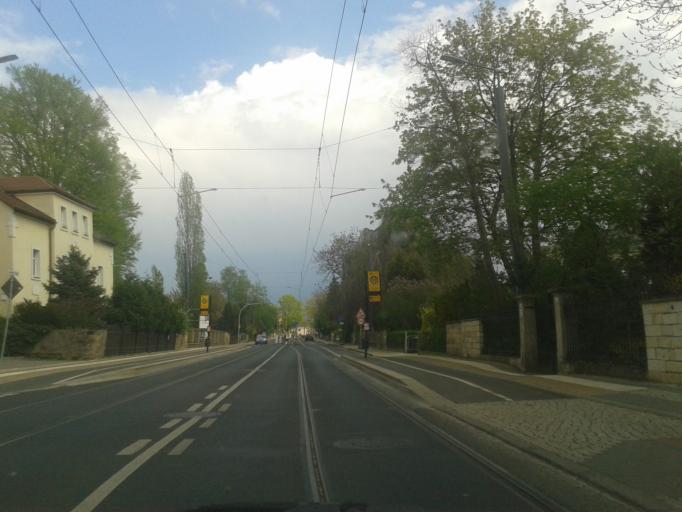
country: DE
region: Saxony
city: Radebeul
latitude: 51.1074
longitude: 13.6350
